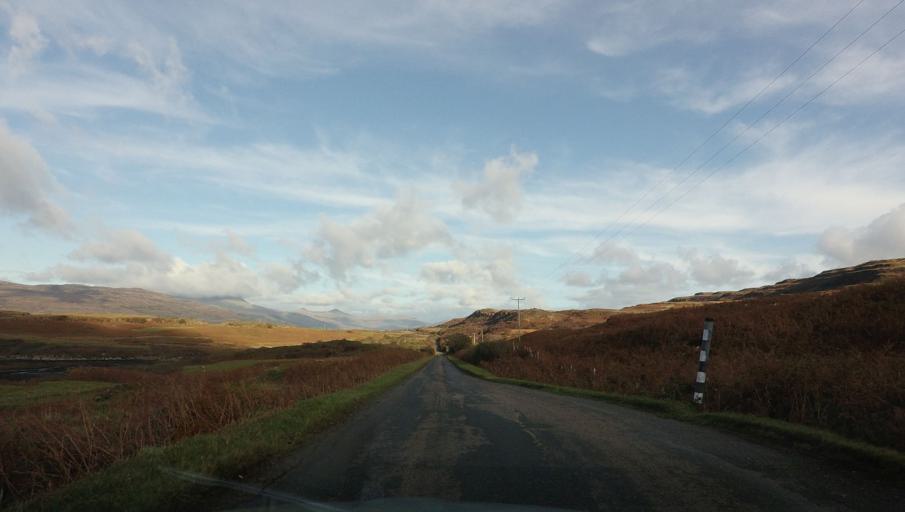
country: GB
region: Scotland
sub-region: Argyll and Bute
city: Isle Of Mull
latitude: 56.3317
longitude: -6.1814
